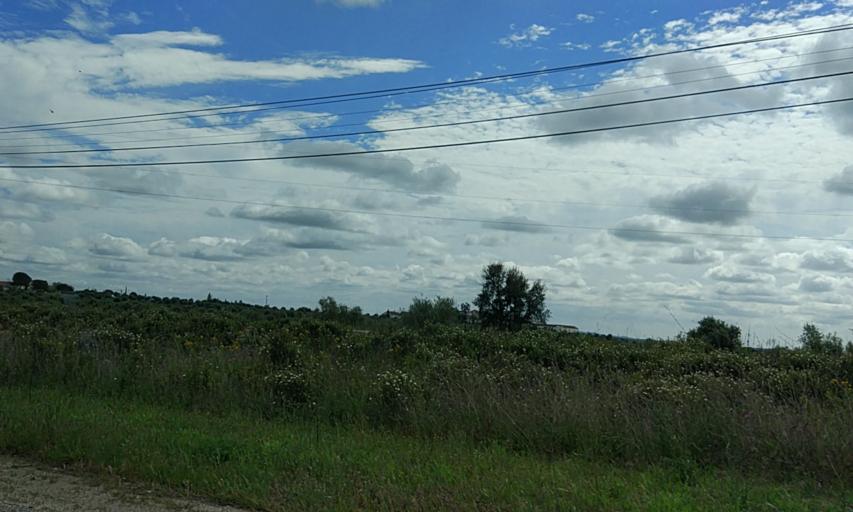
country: PT
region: Evora
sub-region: Vendas Novas
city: Vendas Novas
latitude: 38.6649
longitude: -8.4326
